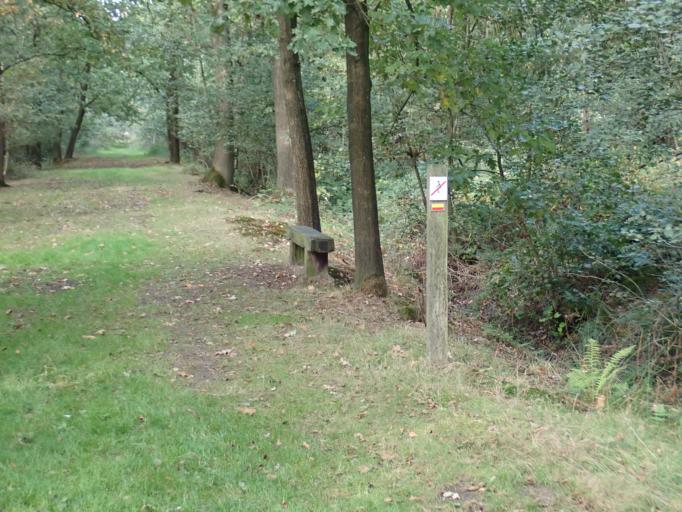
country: NL
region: Zeeland
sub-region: Gemeente Hulst
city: Hulst
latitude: 51.2395
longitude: 4.0681
